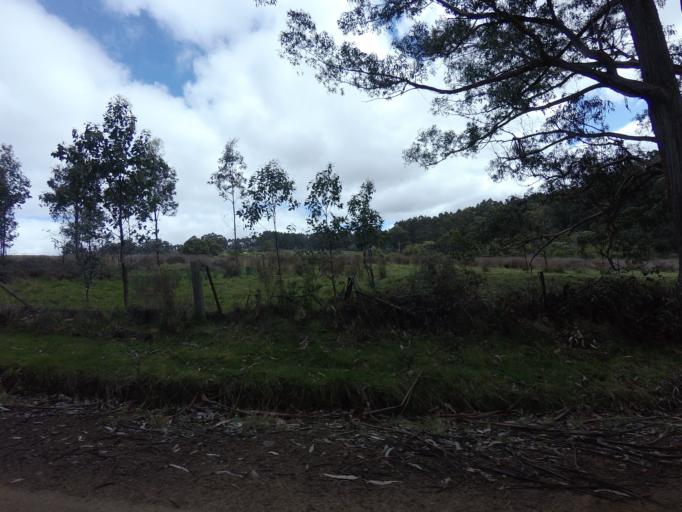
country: AU
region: Tasmania
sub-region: Huon Valley
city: Cygnet
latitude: -43.4086
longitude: 147.0182
